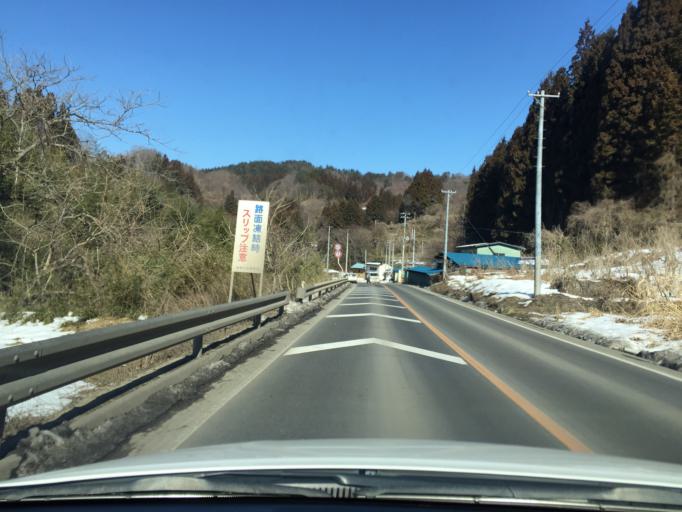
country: JP
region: Fukushima
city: Yanagawamachi-saiwaicho
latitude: 37.7583
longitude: 140.6624
